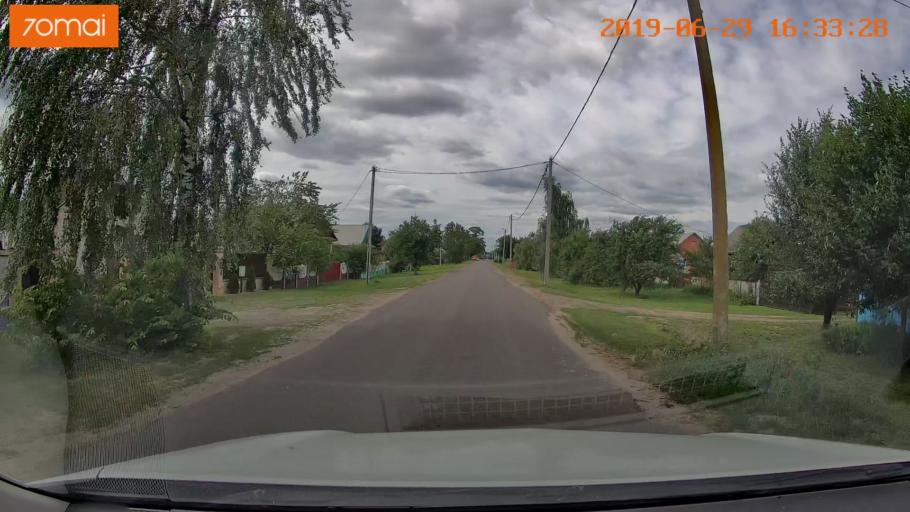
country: BY
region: Brest
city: Luninyets
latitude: 52.2020
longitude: 27.0125
